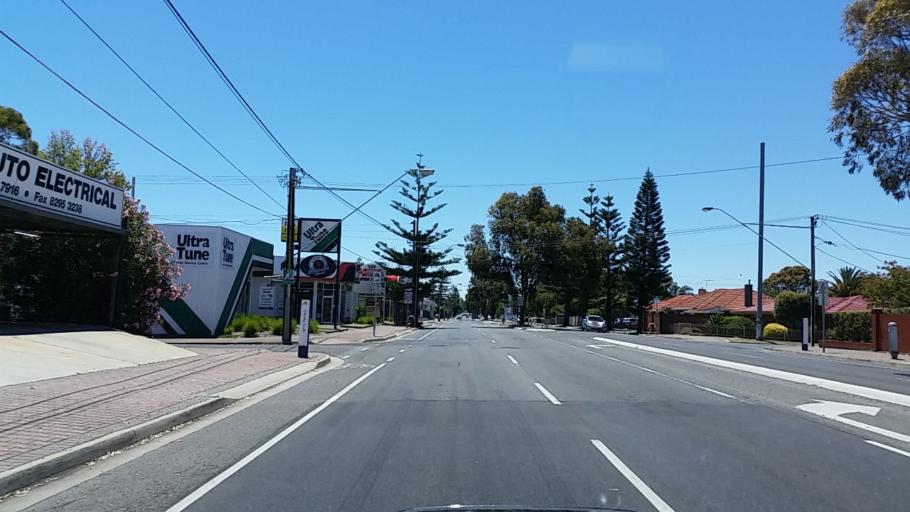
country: AU
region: South Australia
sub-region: Adelaide
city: Glenelg
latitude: -34.9912
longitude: 138.5210
